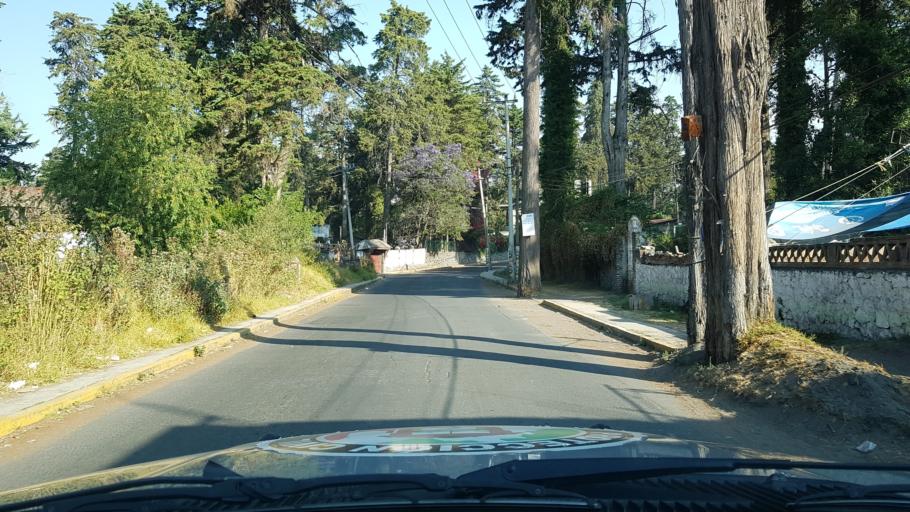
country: MX
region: Mexico
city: Ozumba de Alzate
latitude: 19.0601
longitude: -98.7795
